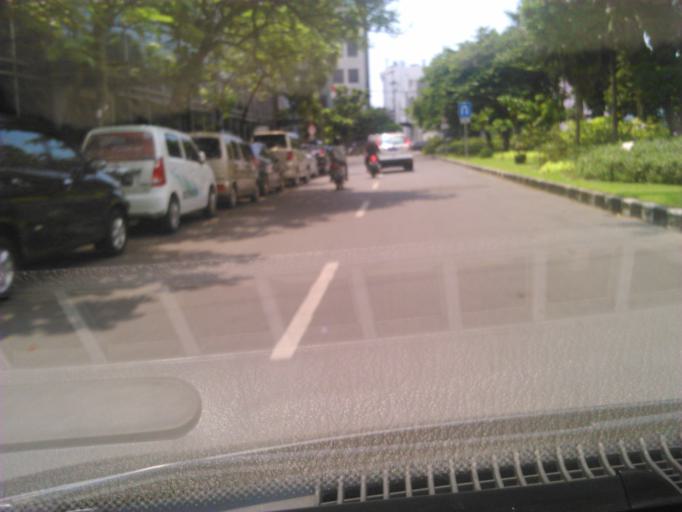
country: ID
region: East Java
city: Gubengairlangga
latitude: -7.2689
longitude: 112.7406
